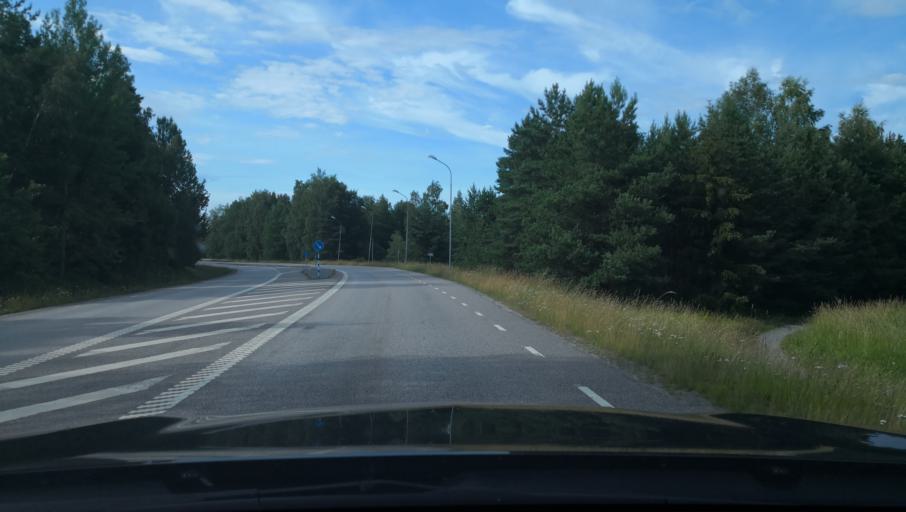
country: SE
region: Uppsala
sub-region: Habo Kommun
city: Balsta
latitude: 59.6036
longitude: 17.5070
